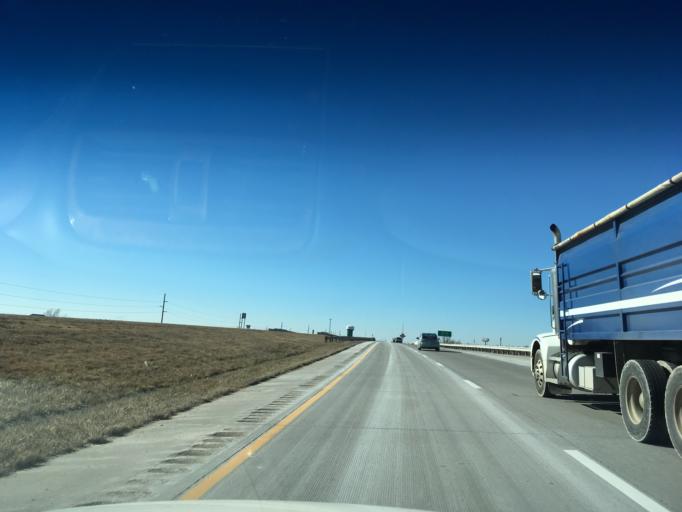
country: US
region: Kansas
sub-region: Reno County
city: South Hutchinson
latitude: 38.0133
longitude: -97.9284
